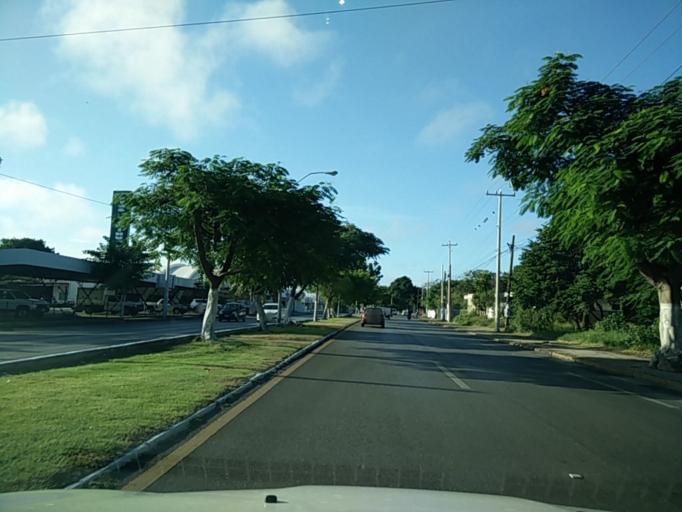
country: MX
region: Yucatan
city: Merida
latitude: 20.9575
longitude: -89.6427
